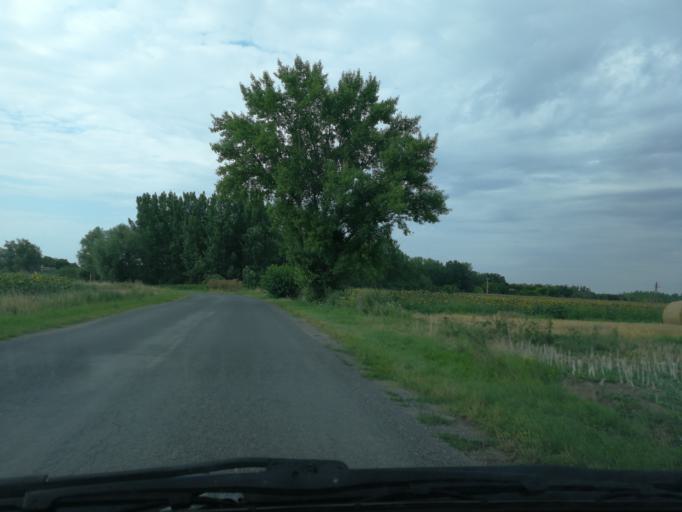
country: HU
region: Bacs-Kiskun
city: Batya
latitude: 46.4529
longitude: 19.0323
